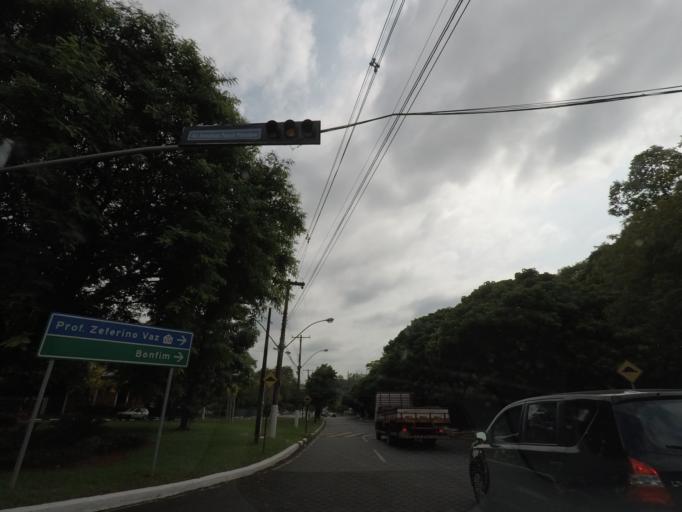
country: BR
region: Sao Paulo
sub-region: Paulinia
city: Paulinia
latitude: -22.7641
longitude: -47.1486
